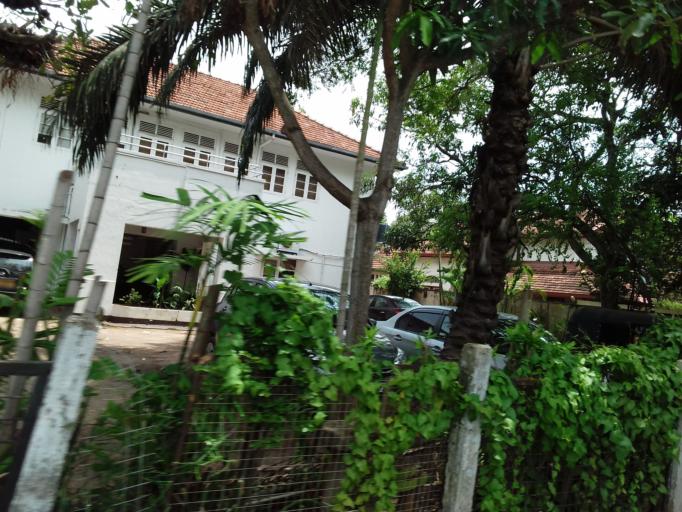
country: LK
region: Western
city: Pita Kotte
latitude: 6.8899
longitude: 79.8616
